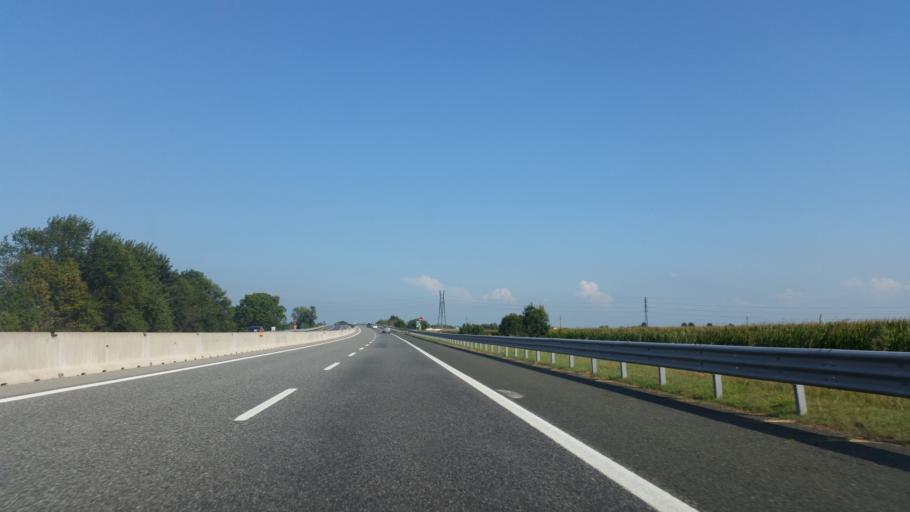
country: IT
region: Piedmont
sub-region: Provincia di Vercelli
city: Santhia
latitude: 45.3571
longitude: 8.1657
